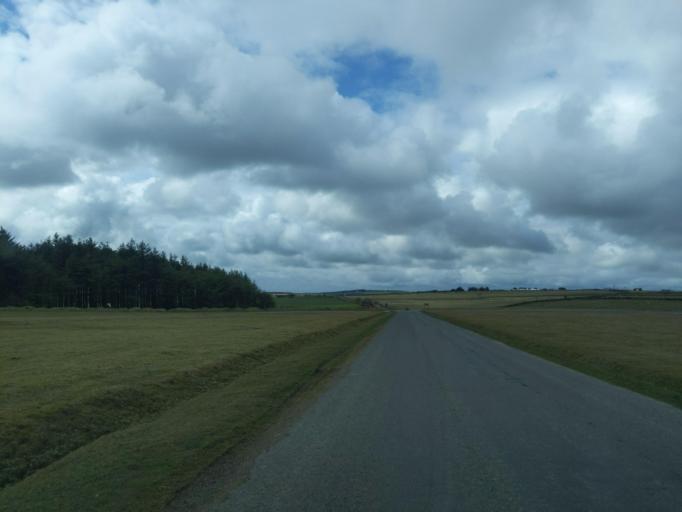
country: GB
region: England
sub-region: Cornwall
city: Camelford
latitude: 50.6393
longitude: -4.6282
